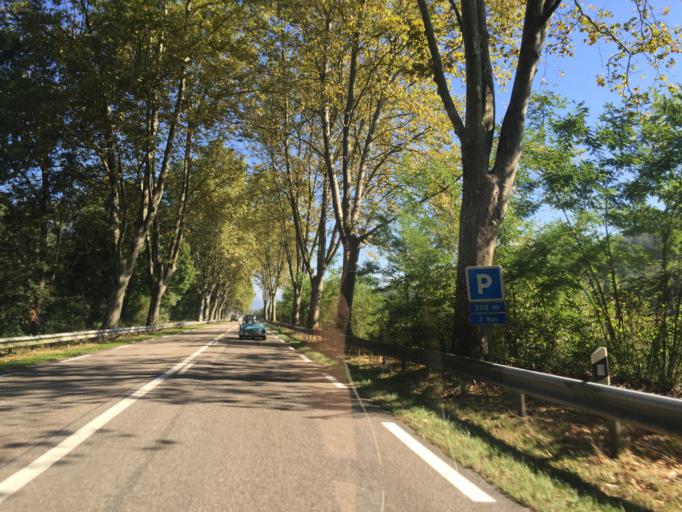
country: FR
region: Rhone-Alpes
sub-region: Departement de la Savoie
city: Cruet
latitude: 45.5231
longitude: 6.1069
